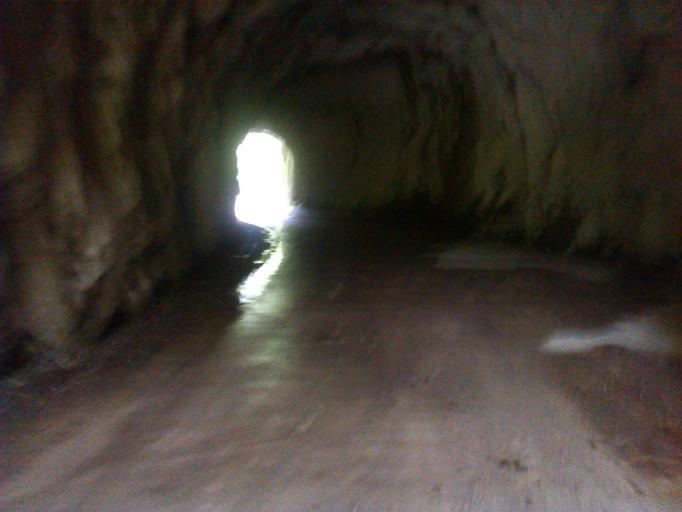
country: ES
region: Basque Country
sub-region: Provincia de Guipuzcoa
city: Berastegui
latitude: 43.1305
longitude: -1.9388
